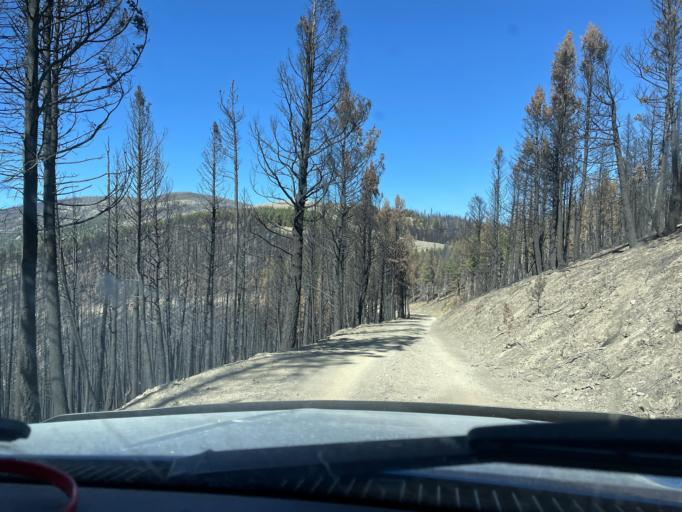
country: US
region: Montana
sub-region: Broadwater County
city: Townsend
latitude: 46.5043
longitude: -111.2754
